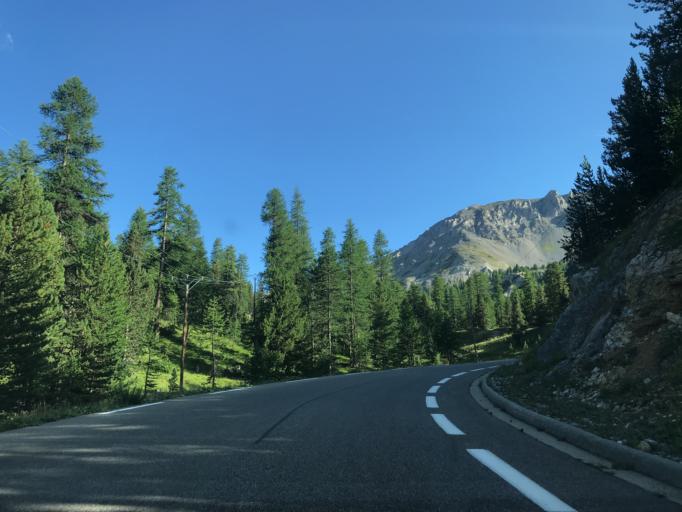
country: FR
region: Provence-Alpes-Cote d'Azur
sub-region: Departement des Hautes-Alpes
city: Villar-Saint-Pancrace
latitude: 44.8317
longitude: 6.7242
